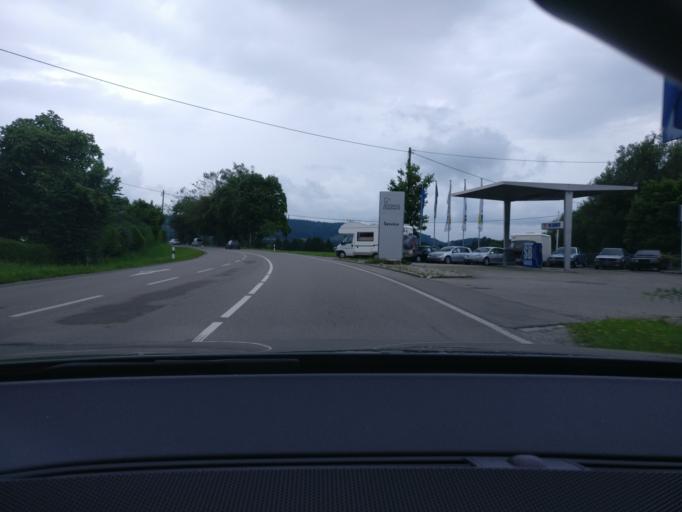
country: DE
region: Bavaria
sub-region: Upper Bavaria
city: Rottenbuch
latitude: 47.7331
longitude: 10.9639
